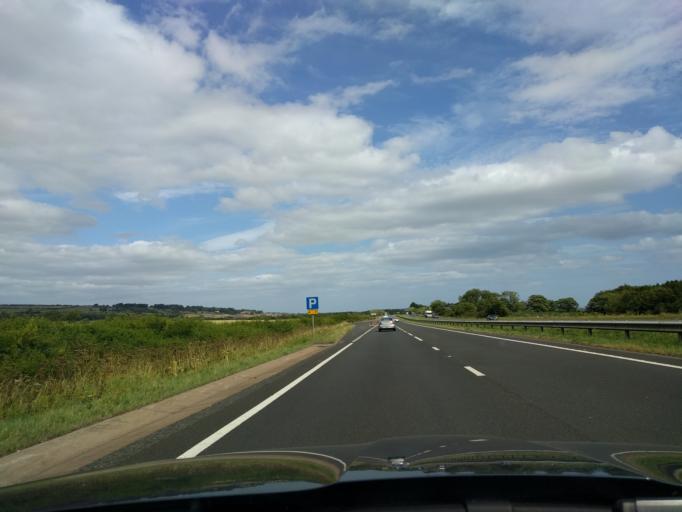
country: GB
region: England
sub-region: Northumberland
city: Alnwick
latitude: 55.3797
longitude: -1.7191
